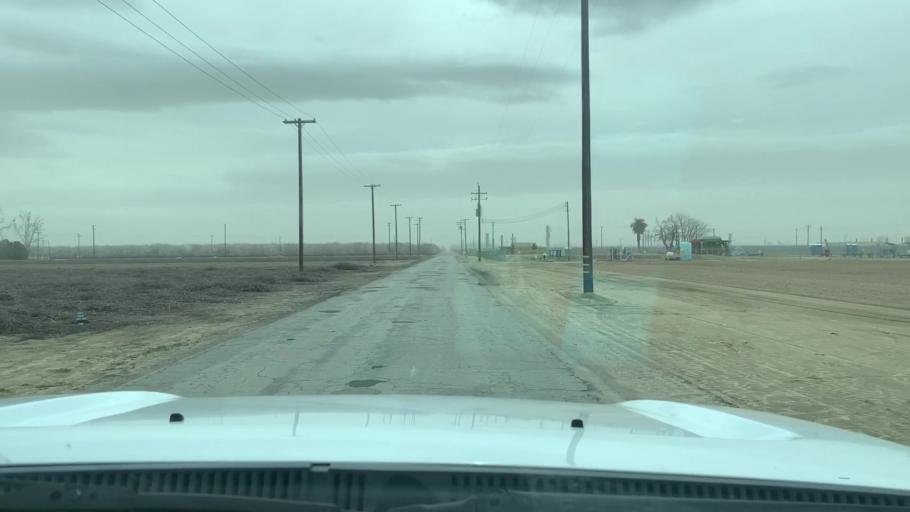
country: US
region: California
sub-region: Kern County
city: Shafter
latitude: 35.5320
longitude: -119.2689
